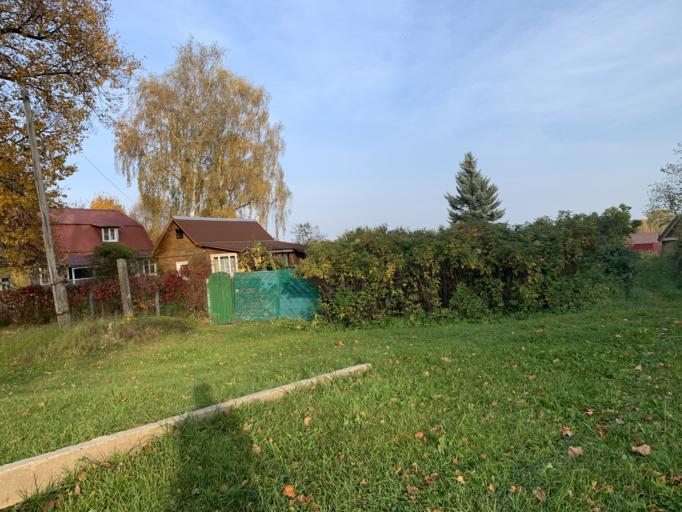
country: RU
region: Jaroslavl
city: Petrovsk
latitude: 56.9798
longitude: 39.3834
